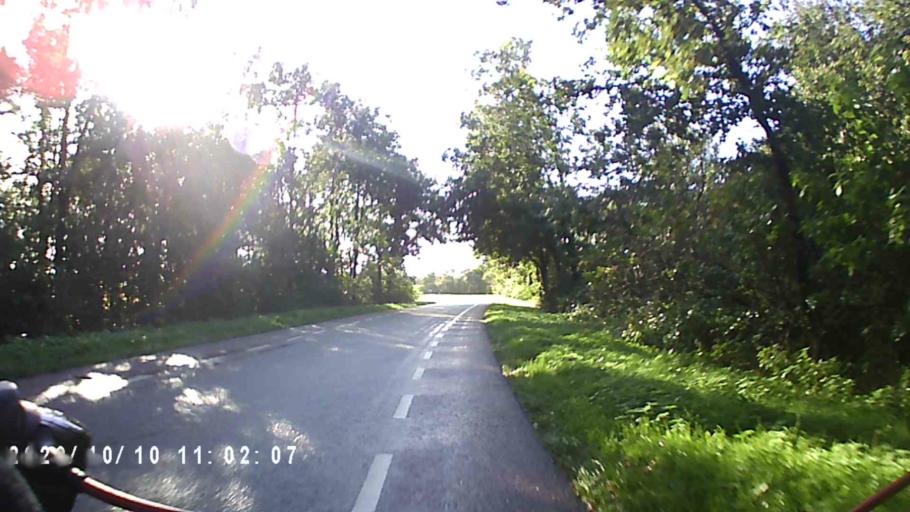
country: NL
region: Friesland
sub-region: Gemeente Achtkarspelen
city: Surhuisterveen
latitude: 53.1381
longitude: 6.2180
